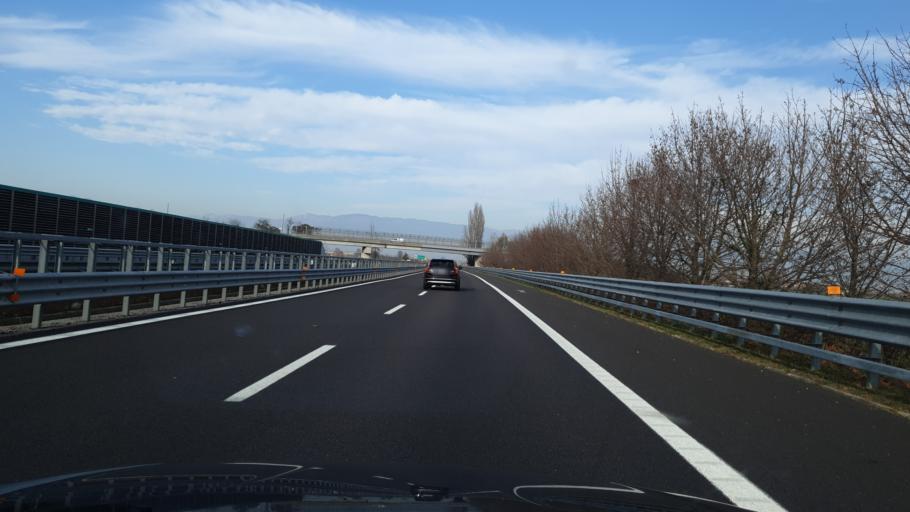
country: IT
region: Veneto
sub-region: Provincia di Vicenza
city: Vigardolo
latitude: 45.6161
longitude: 11.5991
